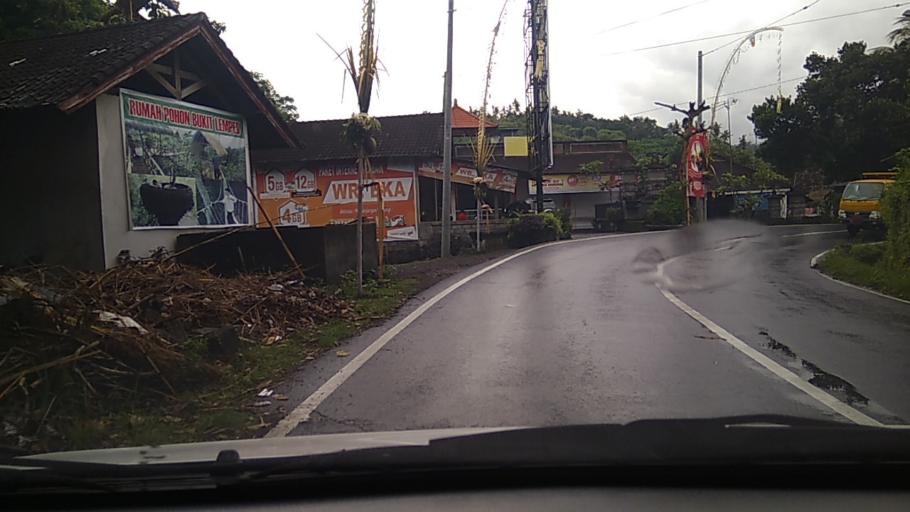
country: ID
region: Bali
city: Banjar Ababi
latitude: -8.4242
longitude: 115.5934
